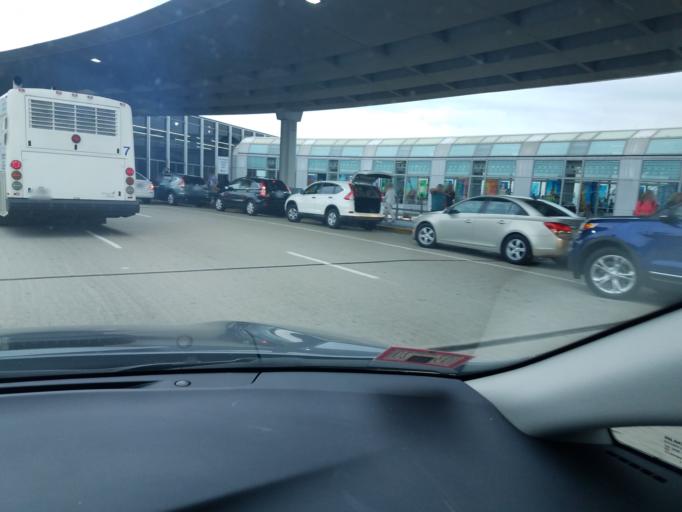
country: US
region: Illinois
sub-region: Cook County
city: Rosemont
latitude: 41.9778
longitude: -87.9062
